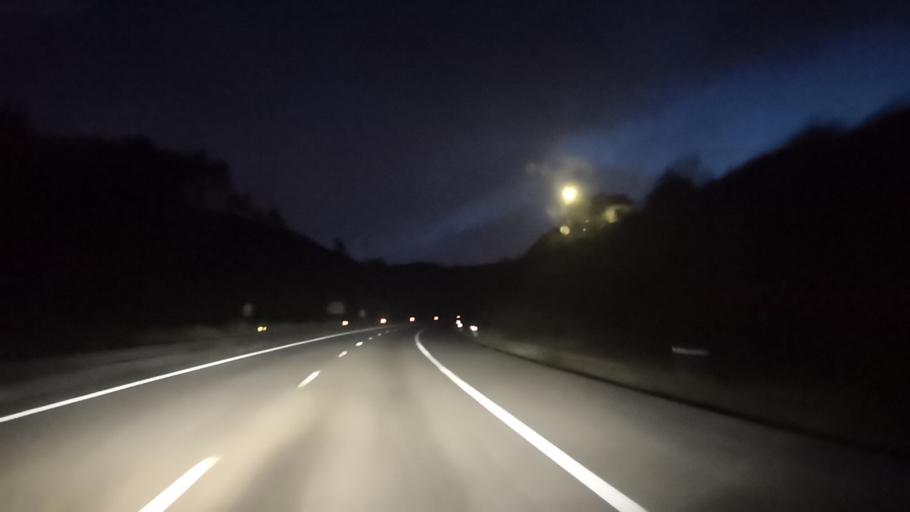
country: PT
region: Porto
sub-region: Lousada
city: Lousada
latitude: 41.3075
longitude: -8.2605
